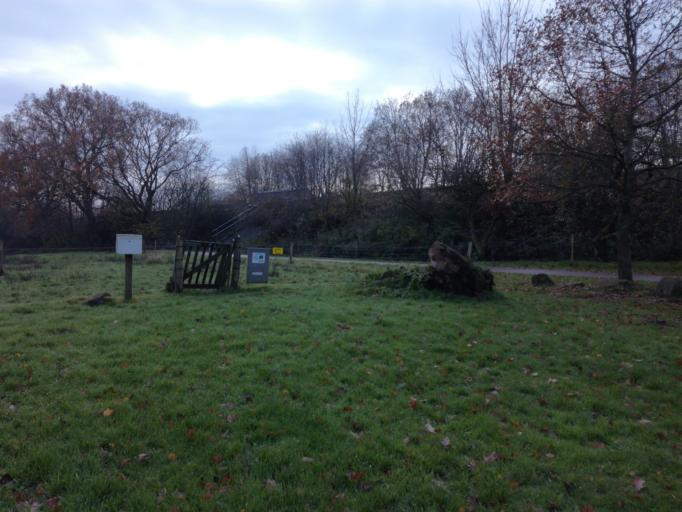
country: DK
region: South Denmark
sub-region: Vejle Kommune
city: Borkop
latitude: 55.6373
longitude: 9.6611
